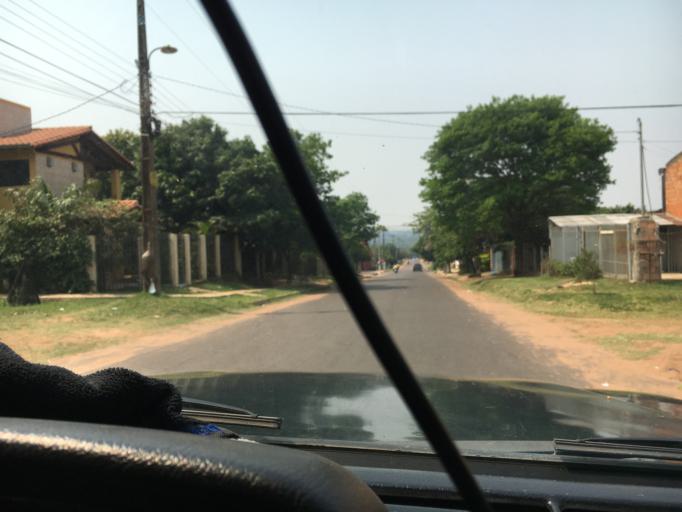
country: PY
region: Central
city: Villa Elisa
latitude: -25.3855
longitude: -57.5808
